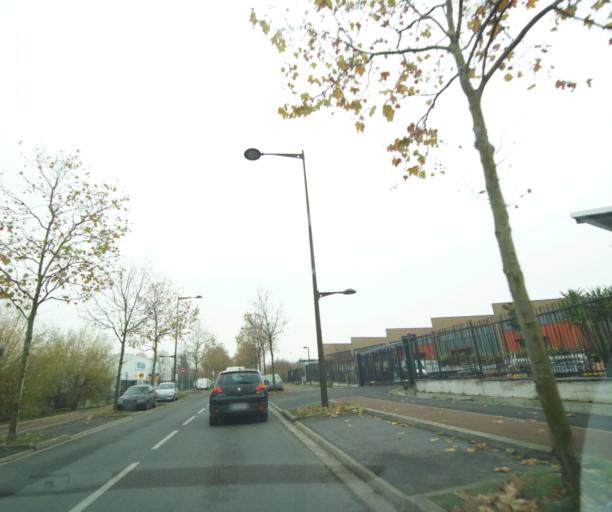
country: FR
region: Ile-de-France
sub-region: Departement de Seine-Saint-Denis
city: Livry-Gargan
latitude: 48.9299
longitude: 2.5479
